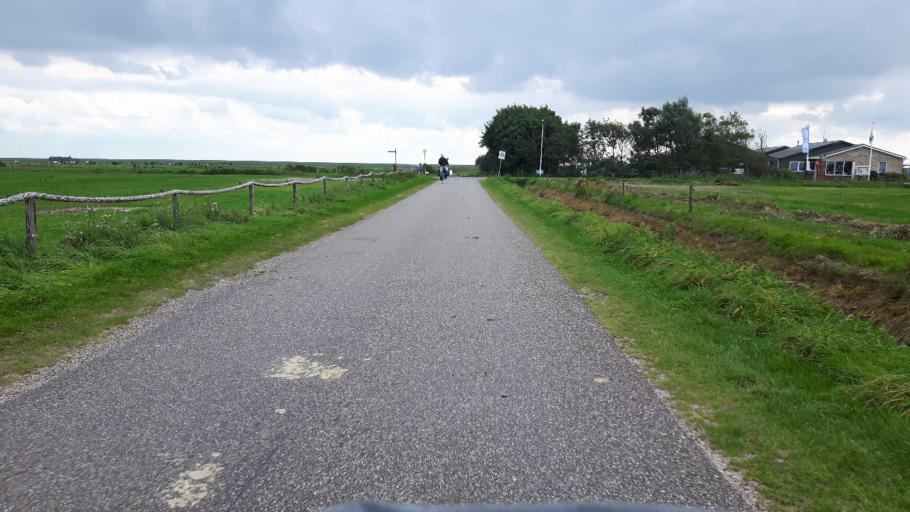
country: NL
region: Friesland
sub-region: Gemeente Ameland
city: Nes
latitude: 53.4504
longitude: 5.8183
